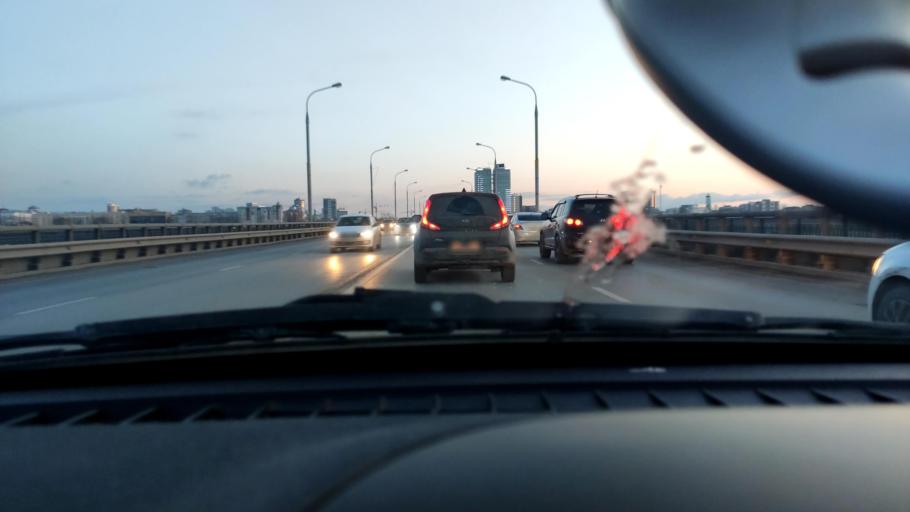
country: RU
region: Perm
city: Perm
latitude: 58.0239
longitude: 56.2199
